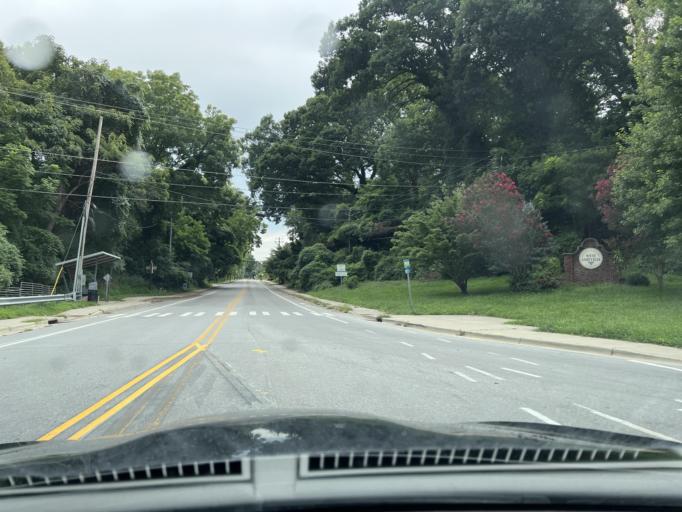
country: US
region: North Carolina
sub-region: Buncombe County
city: Asheville
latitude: 35.5848
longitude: -82.5692
